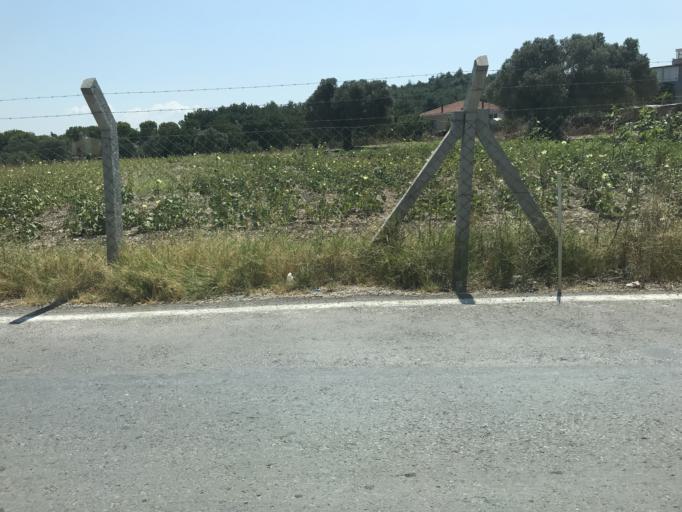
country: TR
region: Izmir
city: Urla
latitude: 38.2714
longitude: 26.7345
